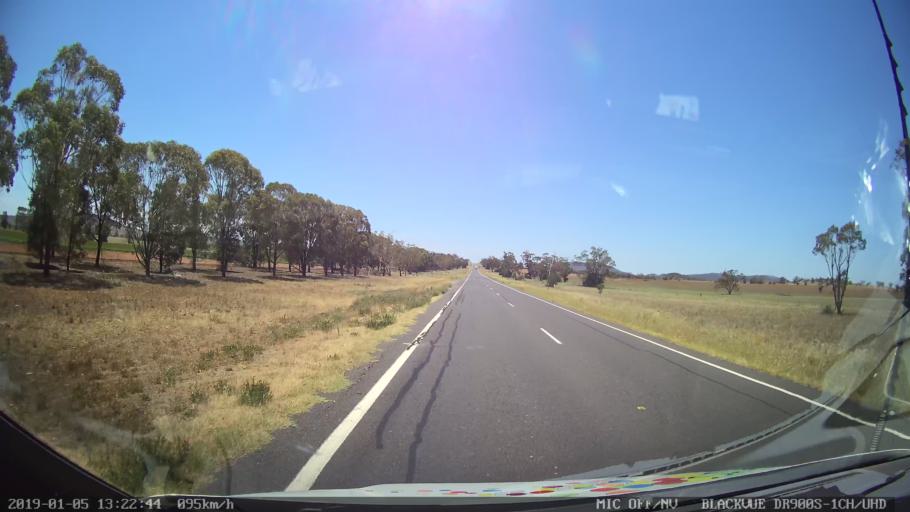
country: AU
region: New South Wales
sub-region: Gunnedah
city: Gunnedah
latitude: -31.0837
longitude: 149.9659
